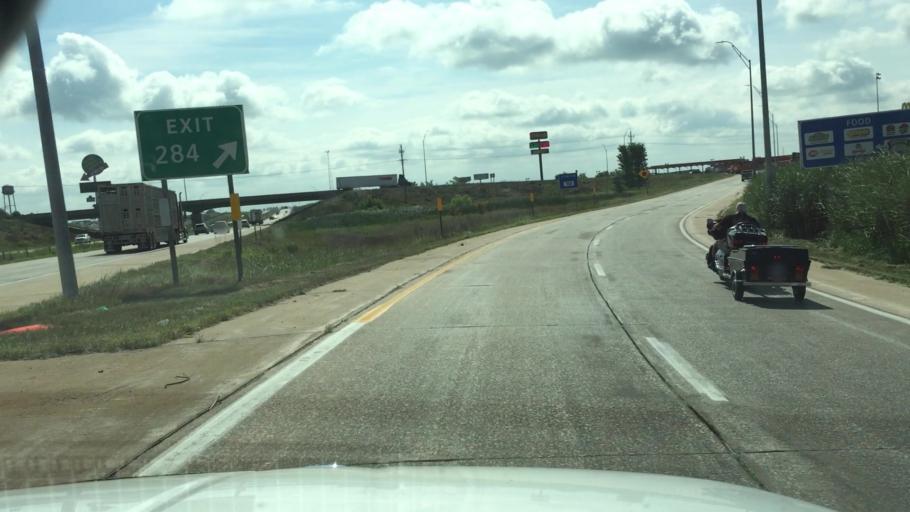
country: US
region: Iowa
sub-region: Scott County
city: Walcott
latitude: 41.6169
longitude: -90.7858
